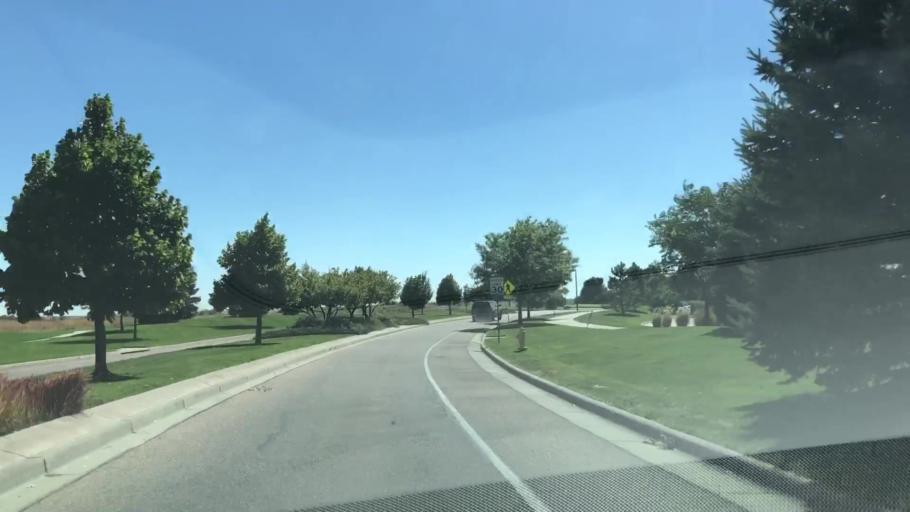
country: US
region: Colorado
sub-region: Weld County
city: Windsor
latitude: 40.5295
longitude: -104.9507
